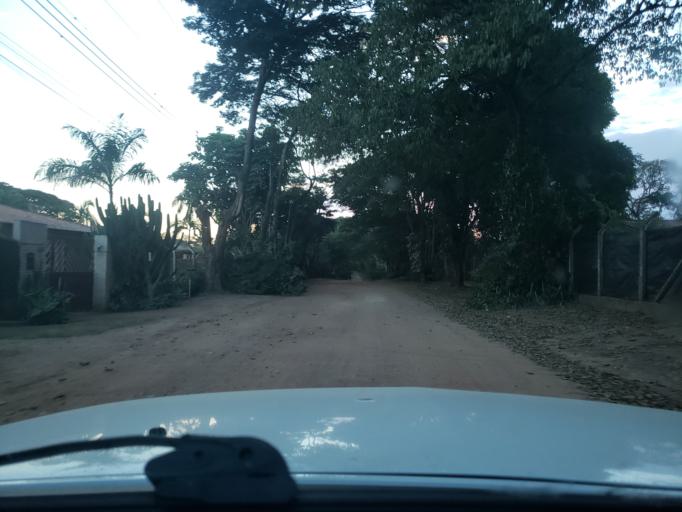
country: BR
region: Sao Paulo
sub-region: Mogi-Mirim
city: Mogi Mirim
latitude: -22.4952
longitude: -46.9787
